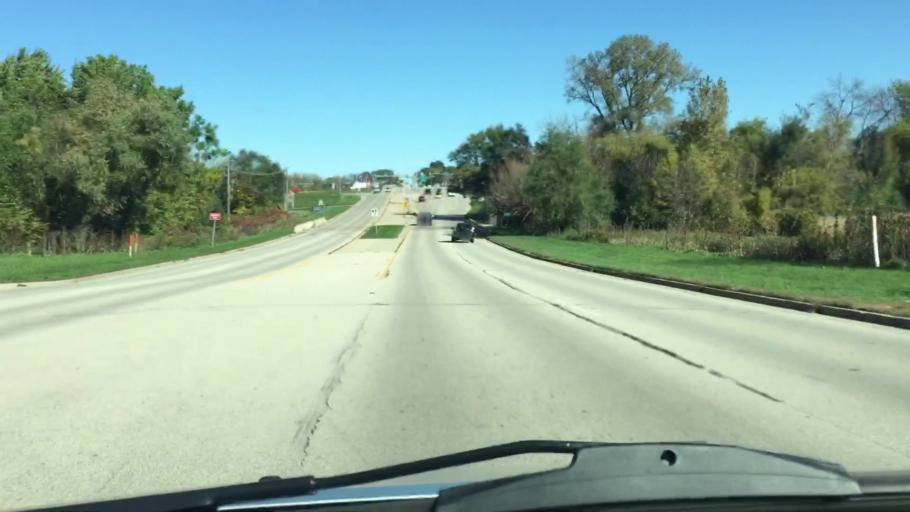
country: US
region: Wisconsin
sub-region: Waukesha County
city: Waukesha
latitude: 43.0452
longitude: -88.2257
